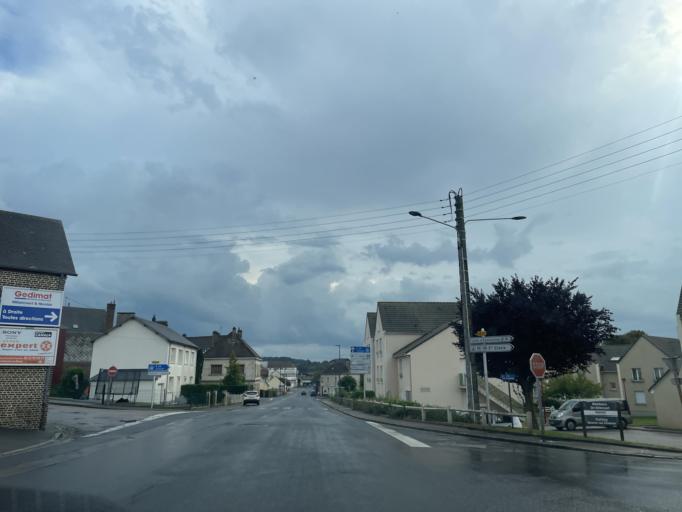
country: FR
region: Haute-Normandie
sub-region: Departement de la Seine-Maritime
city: Neufchatel-en-Bray
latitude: 49.7343
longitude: 1.4370
